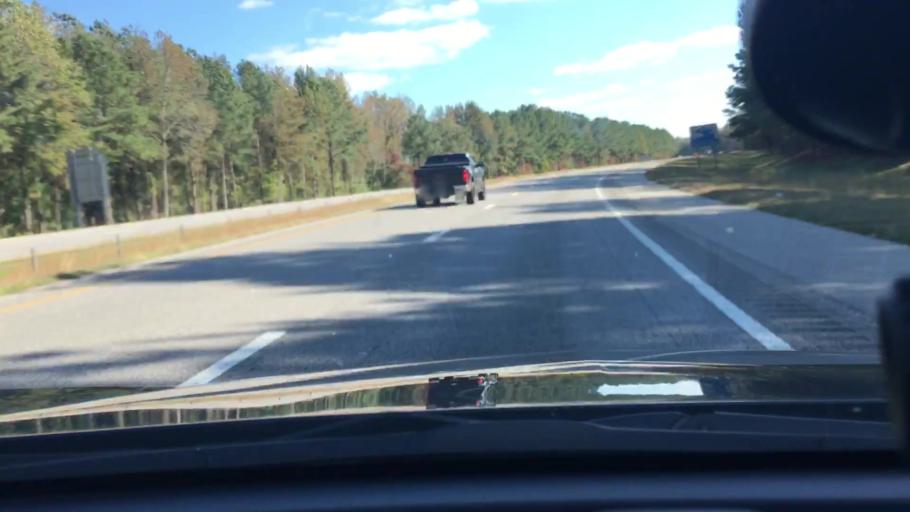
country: US
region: North Carolina
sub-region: Wilson County
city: Wilson
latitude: 35.6782
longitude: -77.8371
